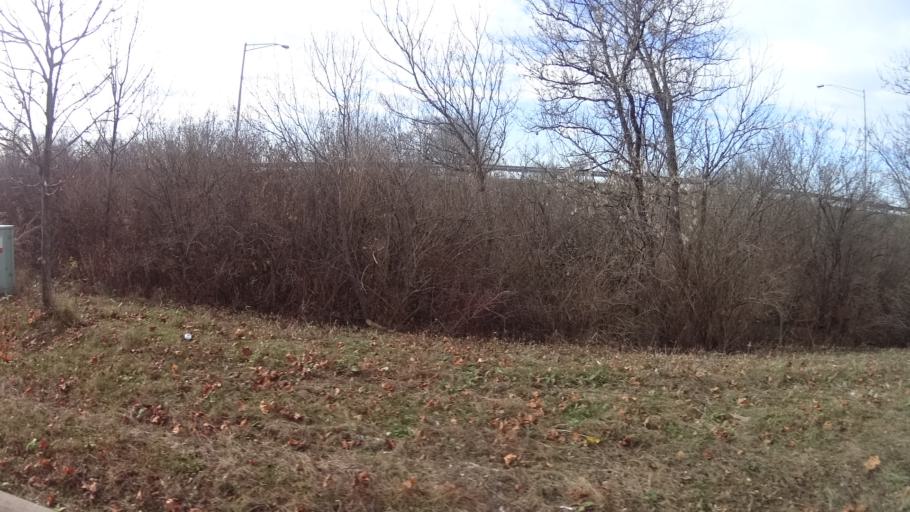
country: US
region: Ohio
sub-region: Lorain County
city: North Ridgeville
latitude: 41.3790
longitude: -81.9818
